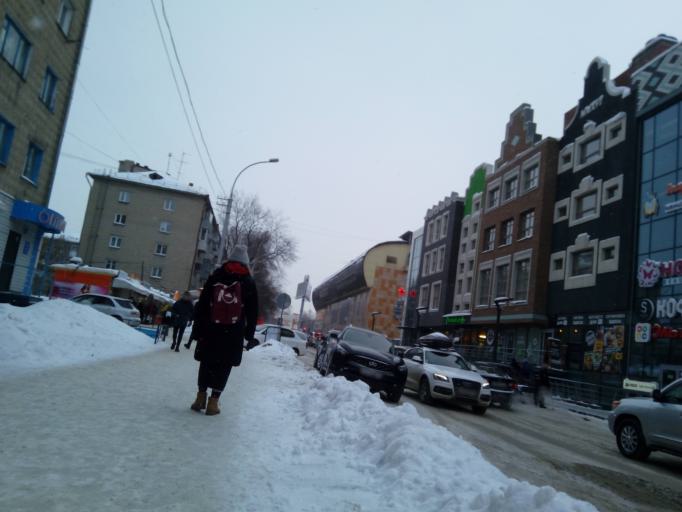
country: RU
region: Novosibirsk
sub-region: Novosibirskiy Rayon
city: Novosibirsk
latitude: 54.9899
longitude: 82.9038
